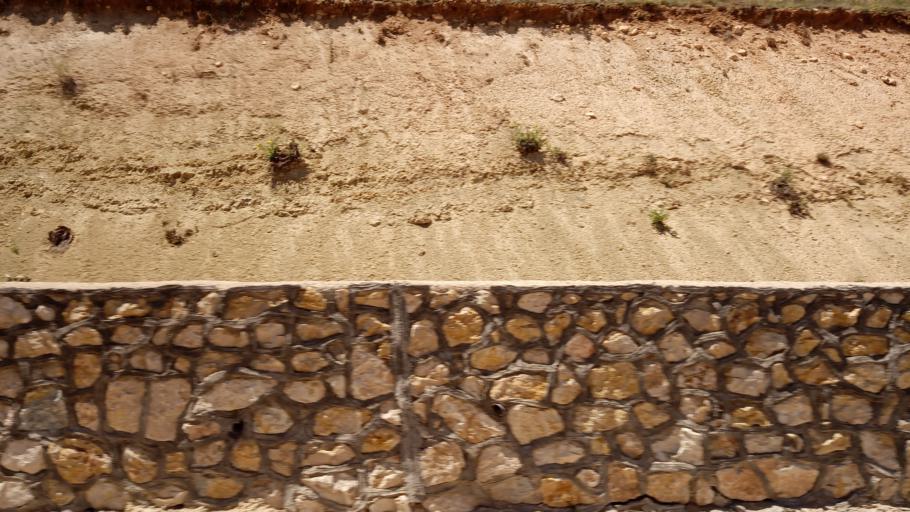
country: TR
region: Malatya
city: Darende
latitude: 38.6124
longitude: 37.4667
